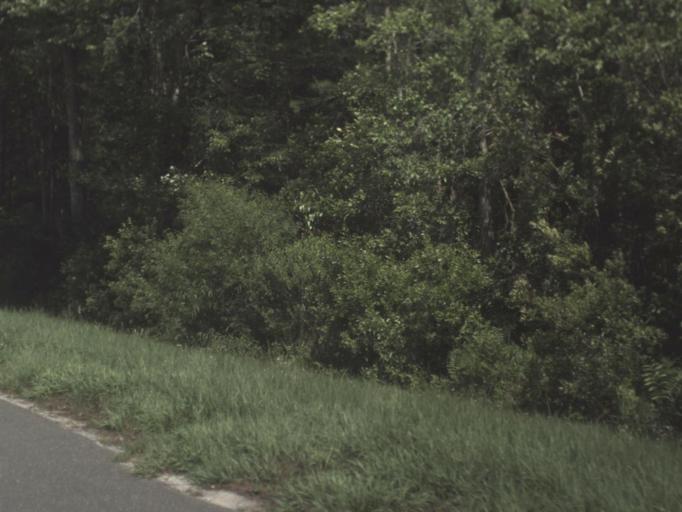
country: US
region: Florida
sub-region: Baker County
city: Macclenny
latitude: 30.2664
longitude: -82.2137
